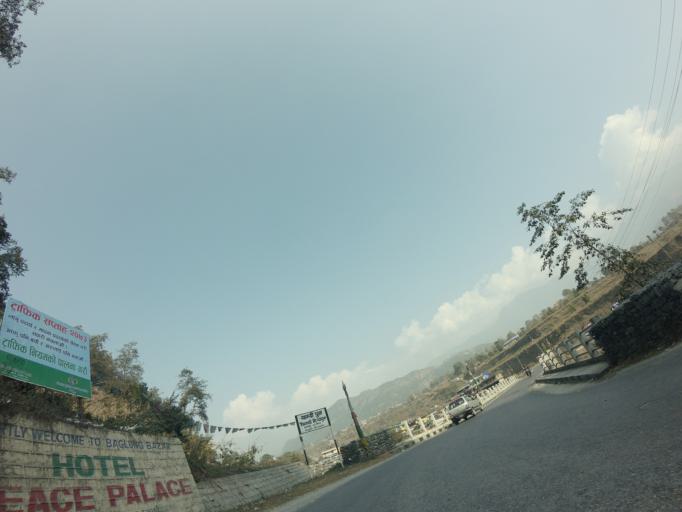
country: NP
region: Western Region
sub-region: Gandaki Zone
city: Pokhara
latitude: 28.2531
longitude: 83.9665
